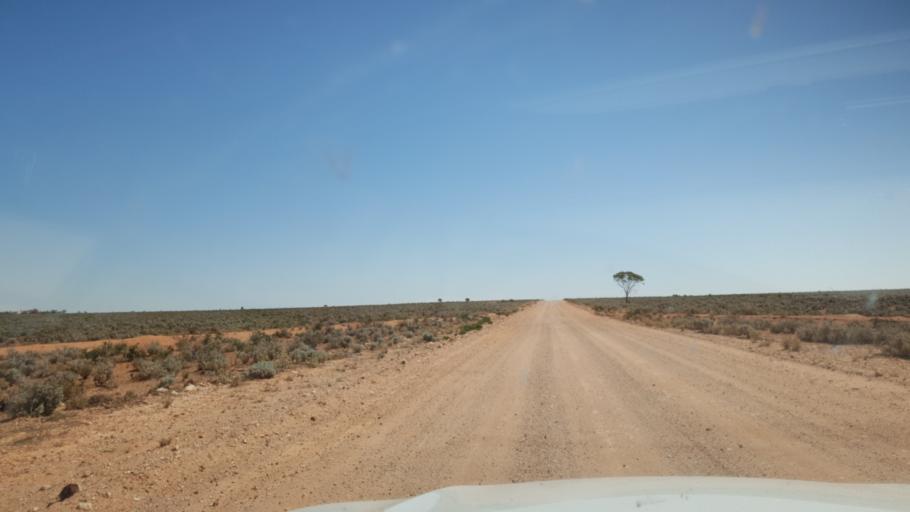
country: AU
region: South Australia
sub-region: Whyalla
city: Whyalla
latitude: -32.6438
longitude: 136.9439
